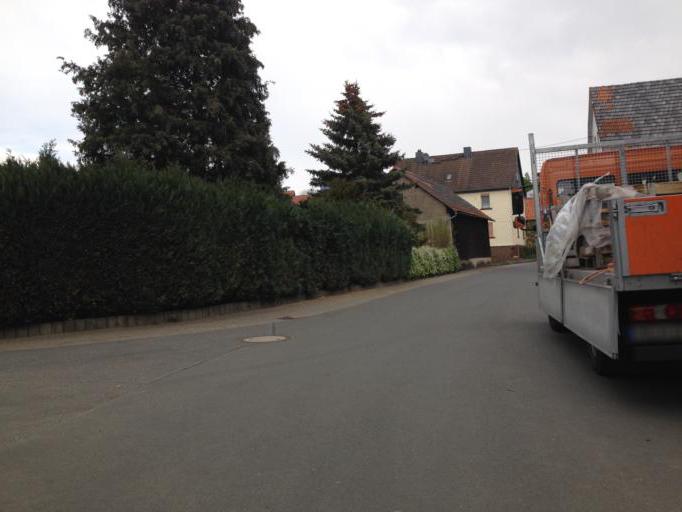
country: DE
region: Hesse
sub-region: Regierungsbezirk Giessen
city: Grunberg
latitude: 50.6348
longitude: 8.9834
